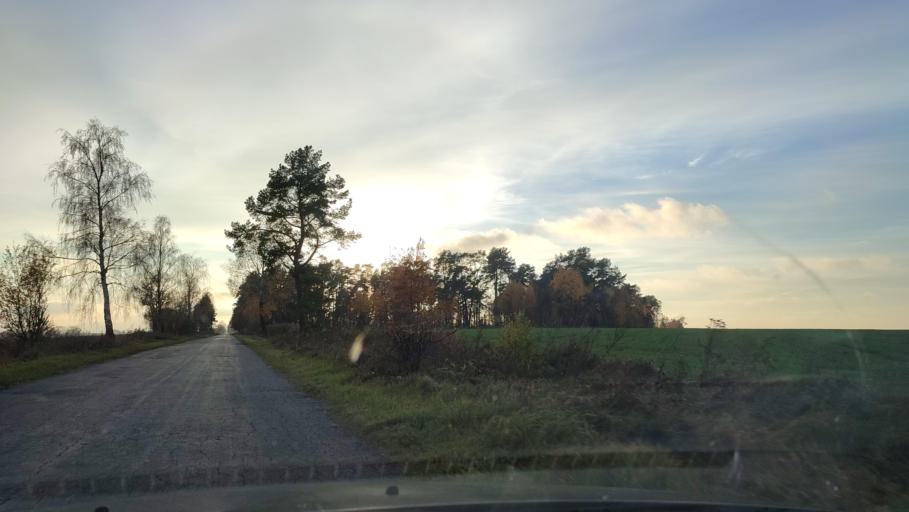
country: PL
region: Masovian Voivodeship
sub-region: Powiat mlawski
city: Dzierzgowo
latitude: 53.2558
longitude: 20.5979
